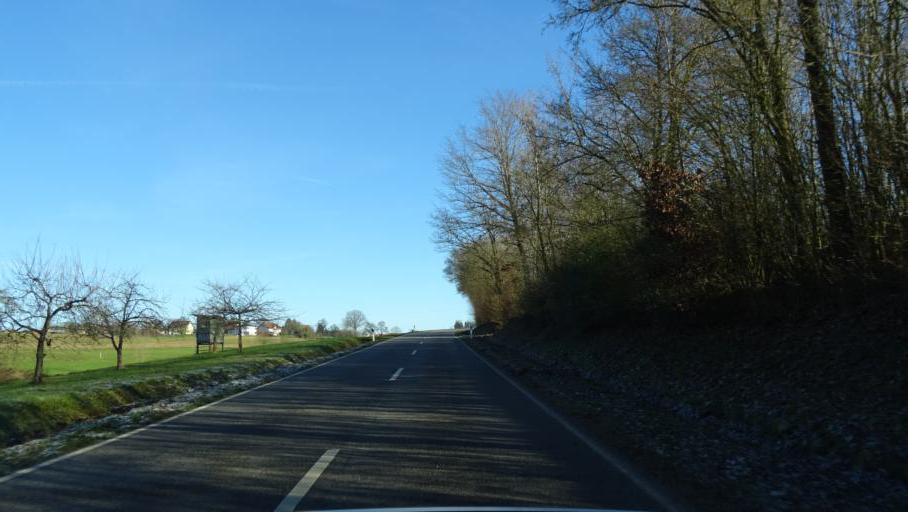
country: DE
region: Baden-Wuerttemberg
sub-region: Karlsruhe Region
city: Fahrenbach
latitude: 49.4041
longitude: 9.1516
